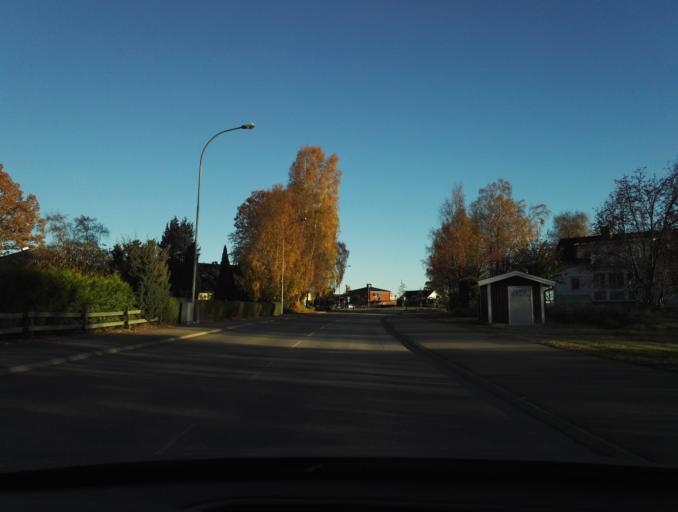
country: SE
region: Kronoberg
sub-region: Vaxjo Kommun
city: Vaexjoe
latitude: 56.8954
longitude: 14.7382
